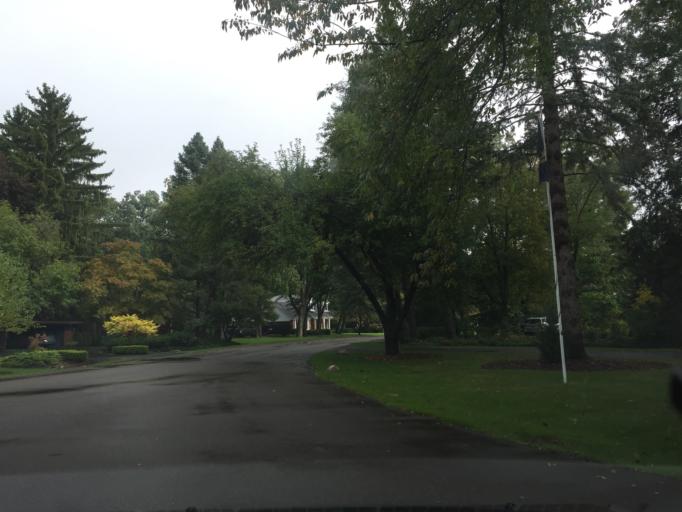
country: US
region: Michigan
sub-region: Oakland County
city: Franklin
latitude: 42.5550
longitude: -83.2889
